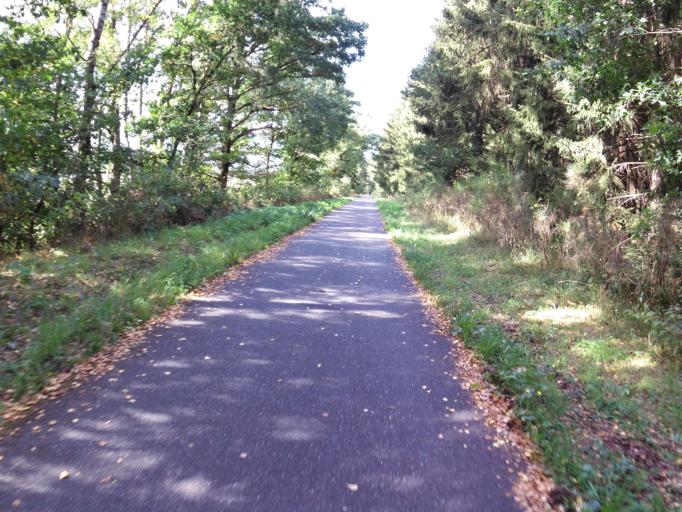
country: DE
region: Rheinland-Pfalz
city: Bleialf
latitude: 50.2134
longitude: 6.2783
